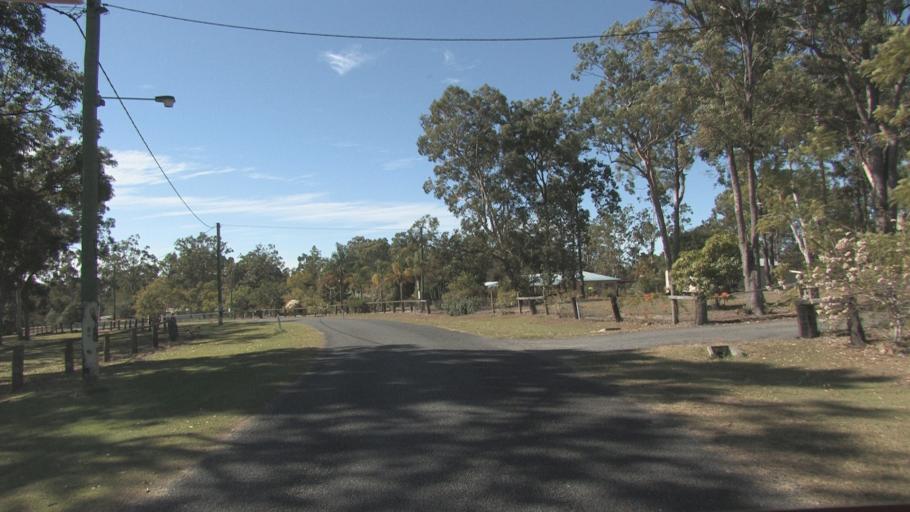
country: AU
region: Queensland
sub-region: Ipswich
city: Springfield Lakes
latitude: -27.7148
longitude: 152.9537
